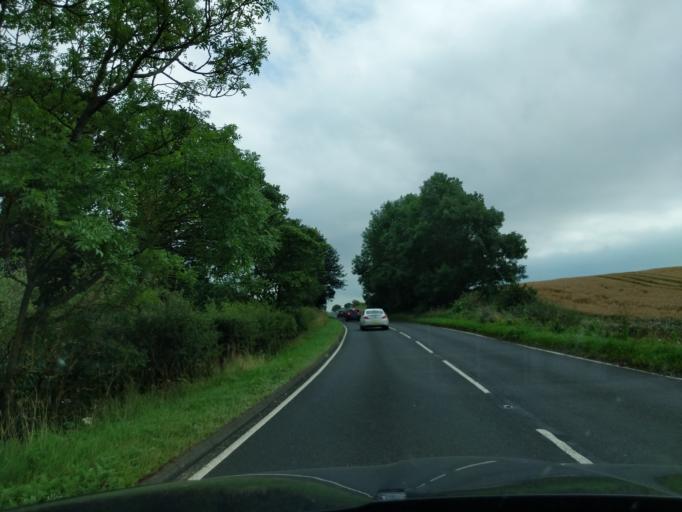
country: GB
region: England
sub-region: Northumberland
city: Whittingham
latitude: 55.4769
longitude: -1.9300
